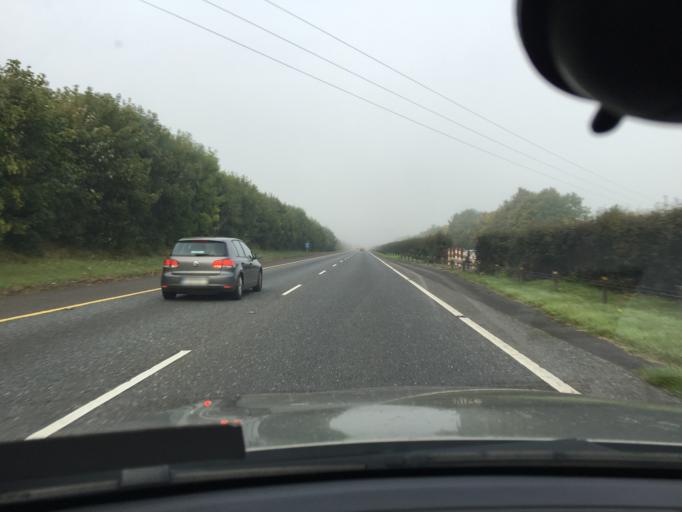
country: IE
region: Leinster
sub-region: Kildare
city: Kilcock
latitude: 53.3776
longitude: -6.6380
